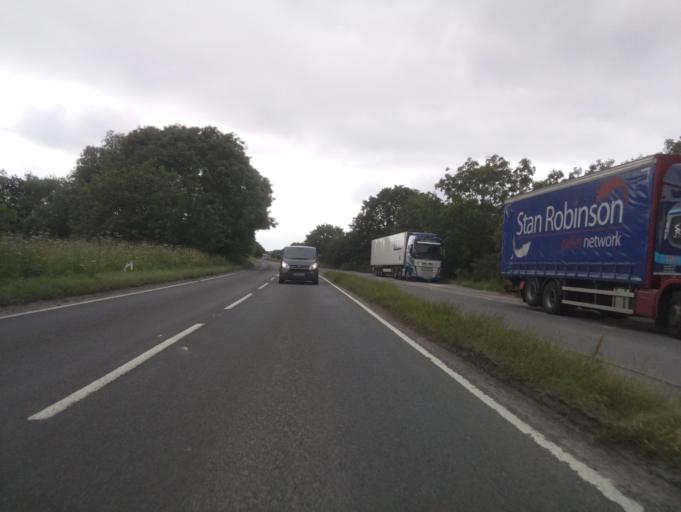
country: GB
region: England
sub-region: Derbyshire
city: Rodsley
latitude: 52.9271
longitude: -1.7624
